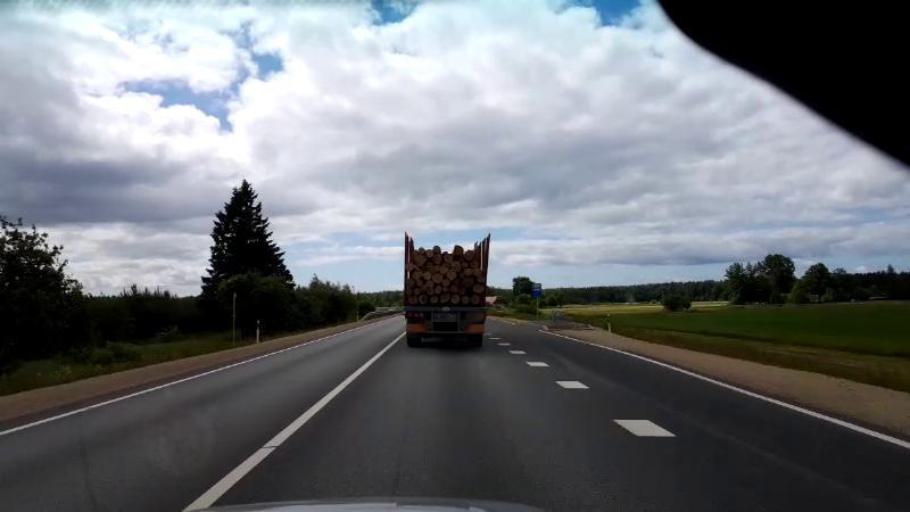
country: LV
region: Salacgrivas
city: Salacgriva
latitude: 57.7192
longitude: 24.3629
